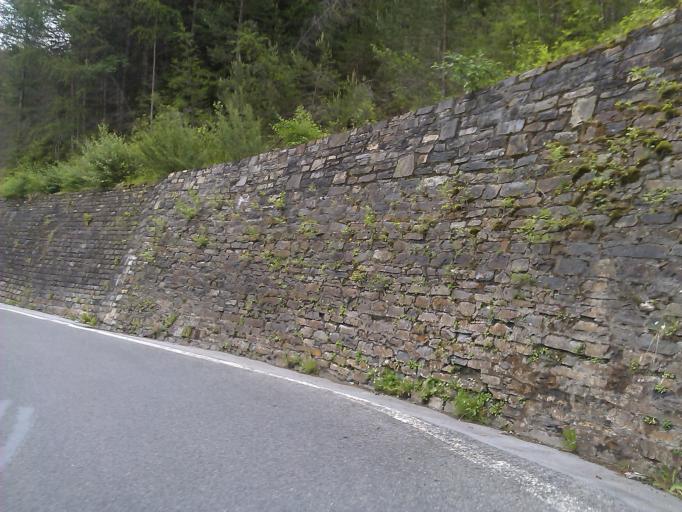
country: AT
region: Tyrol
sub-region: Politischer Bezirk Landeck
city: Nauders
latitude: 46.8854
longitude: 10.4694
